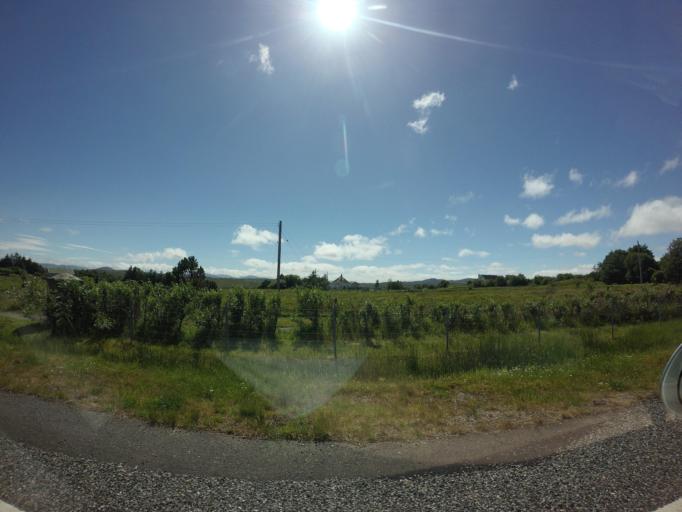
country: GB
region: Scotland
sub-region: Eilean Siar
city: Harris
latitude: 58.1921
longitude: -6.7095
